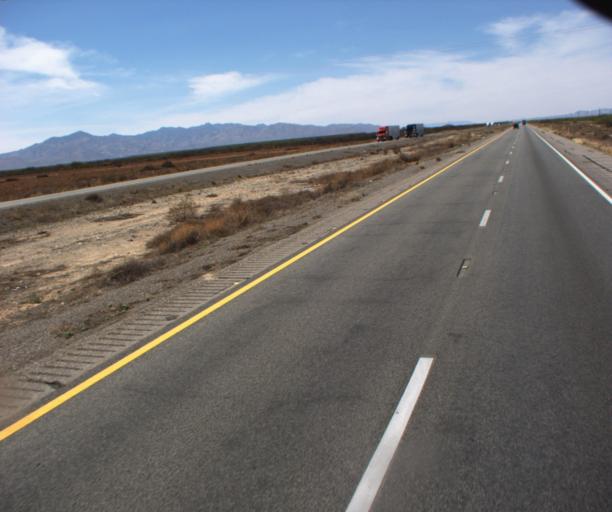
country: US
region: Arizona
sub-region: Cochise County
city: Willcox
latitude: 32.2855
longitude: -109.3015
